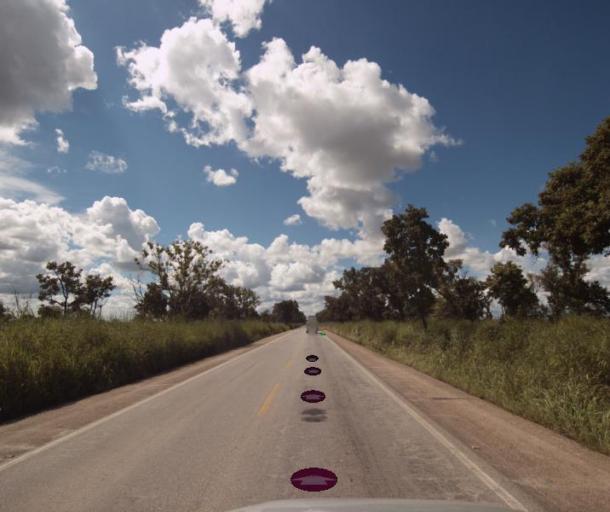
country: BR
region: Goias
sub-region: Porangatu
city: Porangatu
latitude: -13.6140
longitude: -49.0423
